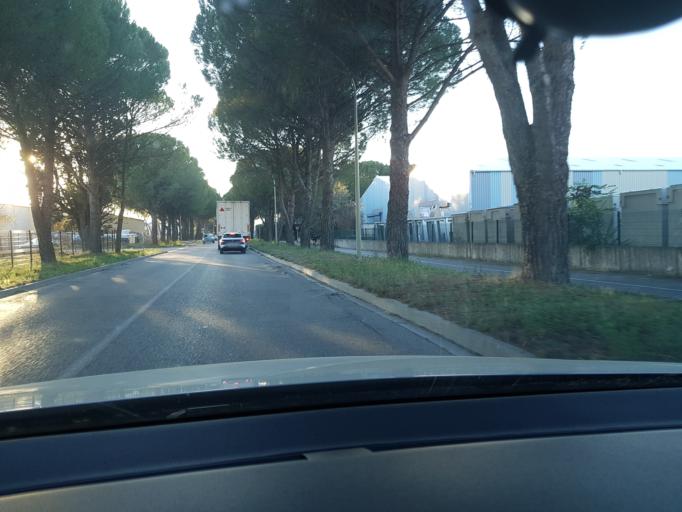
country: FR
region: Provence-Alpes-Cote d'Azur
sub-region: Departement des Bouches-du-Rhone
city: Rousset
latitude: 43.4689
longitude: 5.6092
